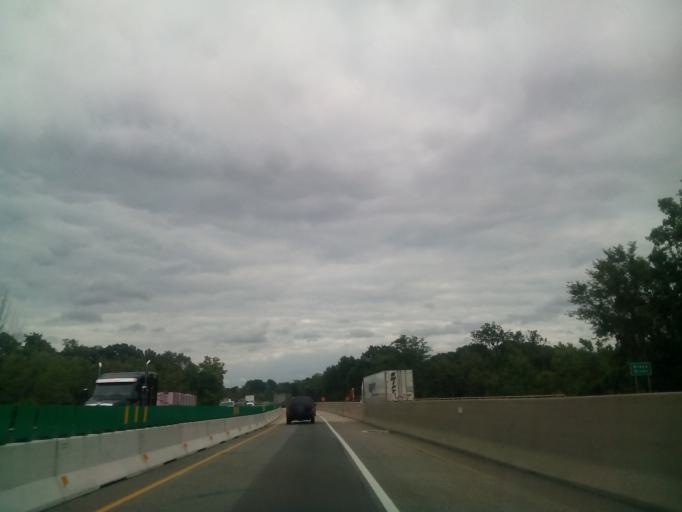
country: US
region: Ohio
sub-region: Lorain County
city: Elyria
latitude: 41.3850
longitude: -82.1049
